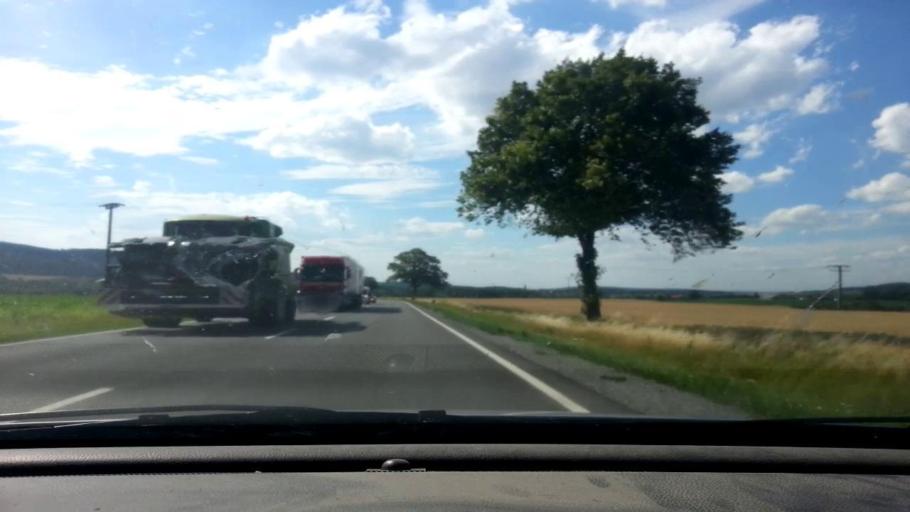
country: DE
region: Bavaria
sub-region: Upper Franconia
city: Emtmannsberg
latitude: 49.9063
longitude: 11.6796
